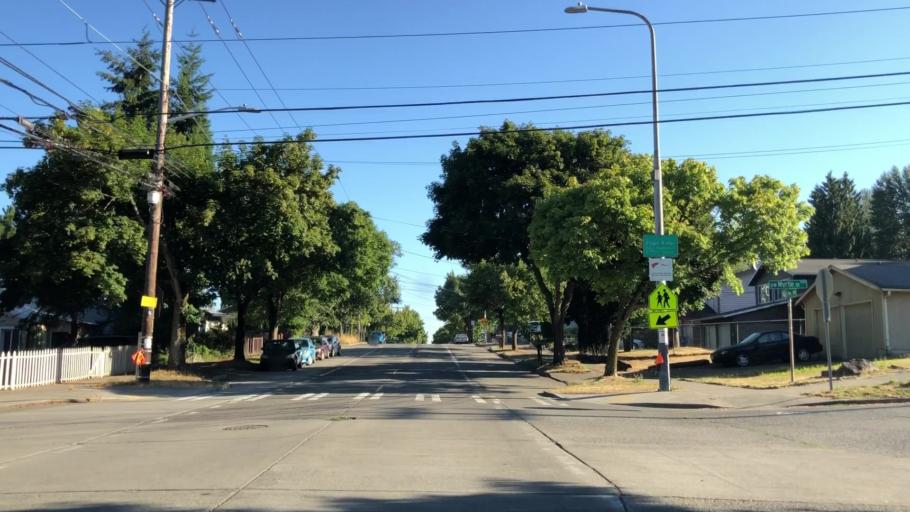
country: US
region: Washington
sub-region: King County
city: White Center
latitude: 47.5390
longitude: -122.3551
